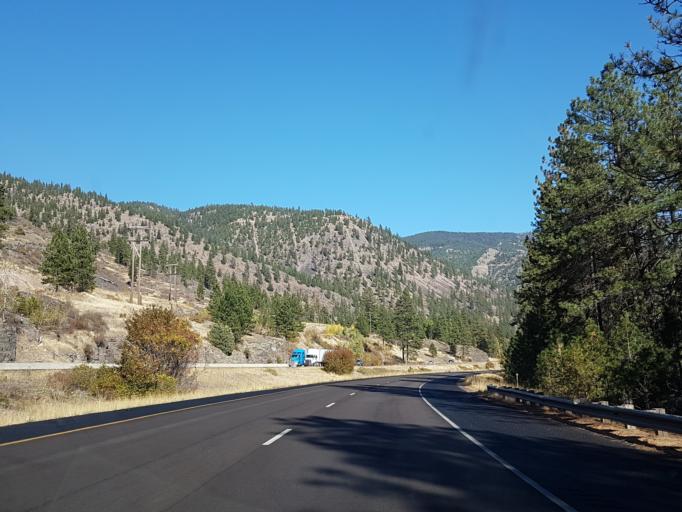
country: US
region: Montana
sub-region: Missoula County
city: Frenchtown
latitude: 47.0195
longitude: -114.5357
